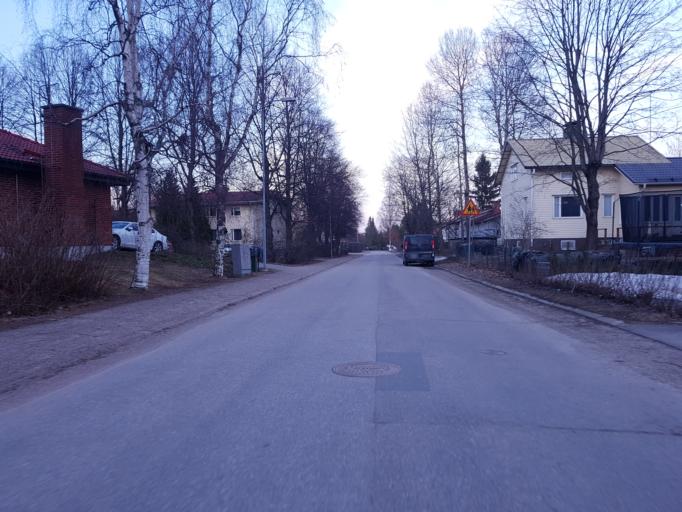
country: FI
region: Uusimaa
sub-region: Helsinki
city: Helsinki
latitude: 60.2595
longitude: 24.9545
